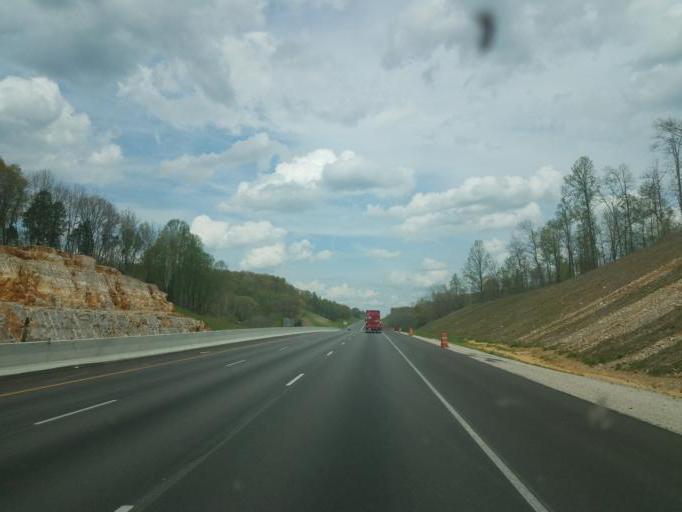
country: US
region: Kentucky
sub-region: Hart County
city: Munfordville
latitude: 37.3066
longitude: -85.9030
